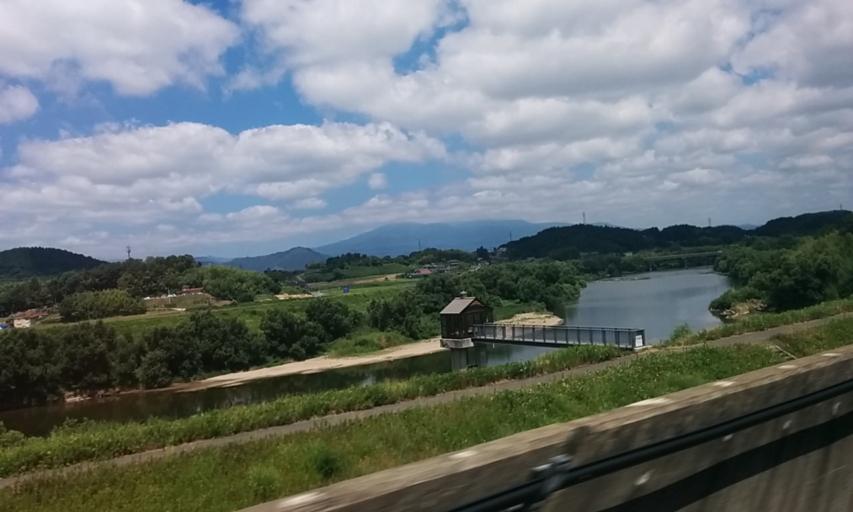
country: JP
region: Fukushima
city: Motomiya
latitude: 37.4700
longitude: 140.4136
